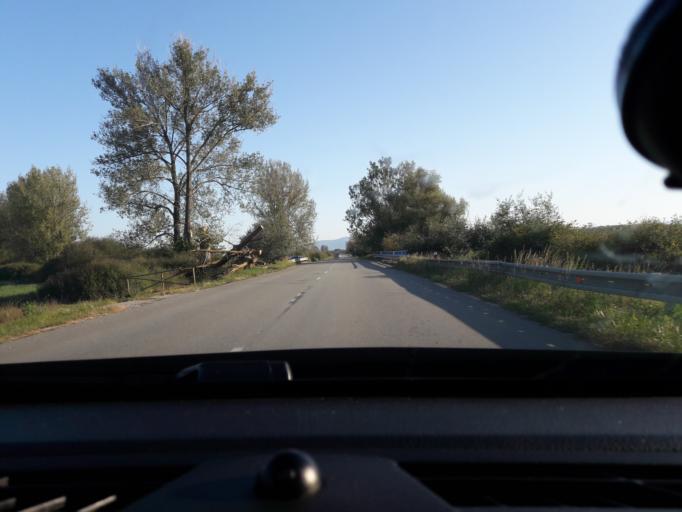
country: SK
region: Kosicky
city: Michalovce
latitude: 48.6542
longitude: 21.9390
